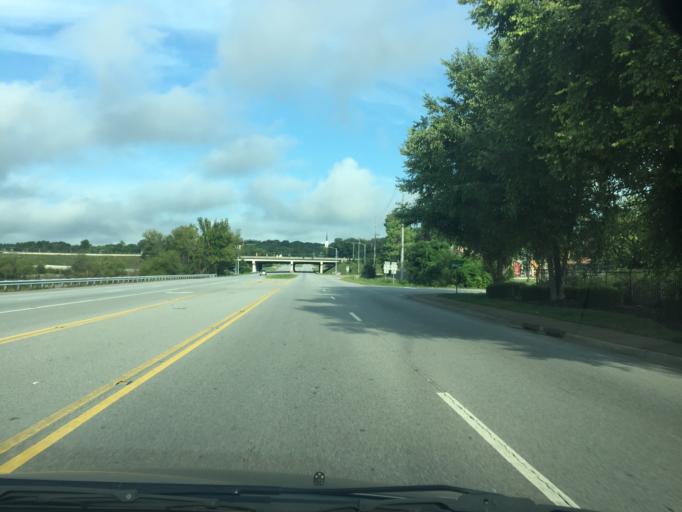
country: US
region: Tennessee
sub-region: Hamilton County
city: East Chattanooga
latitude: 35.0746
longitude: -85.1956
